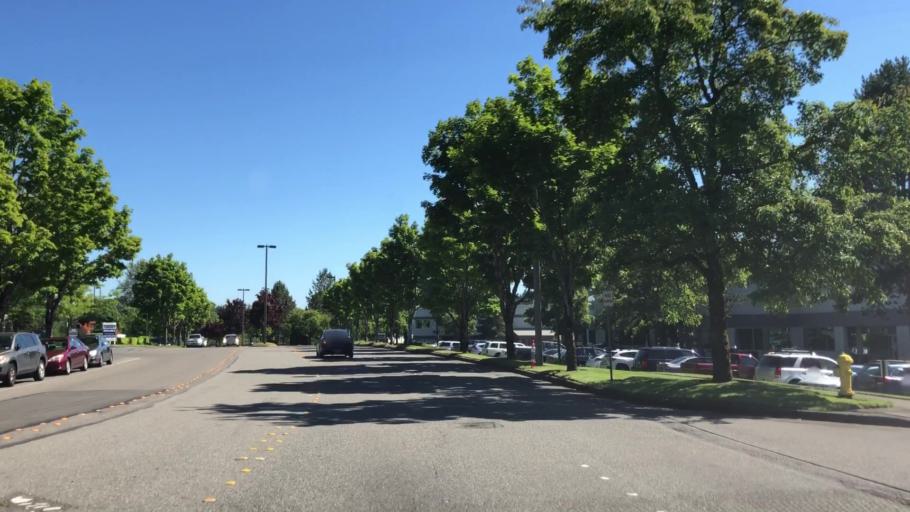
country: US
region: Washington
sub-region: Snohomish County
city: North Creek
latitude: 47.7981
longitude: -122.1987
